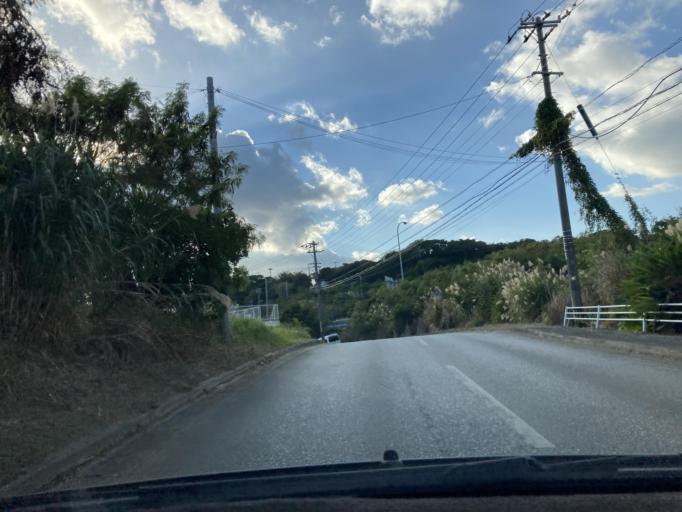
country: JP
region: Okinawa
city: Chatan
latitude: 26.2882
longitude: 127.7886
